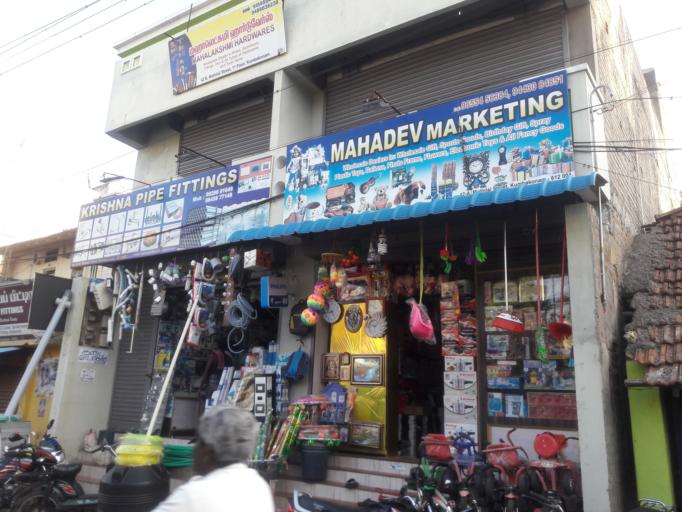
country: IN
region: Tamil Nadu
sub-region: Thanjavur
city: Kumbakonam
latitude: 10.9603
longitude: 79.3878
